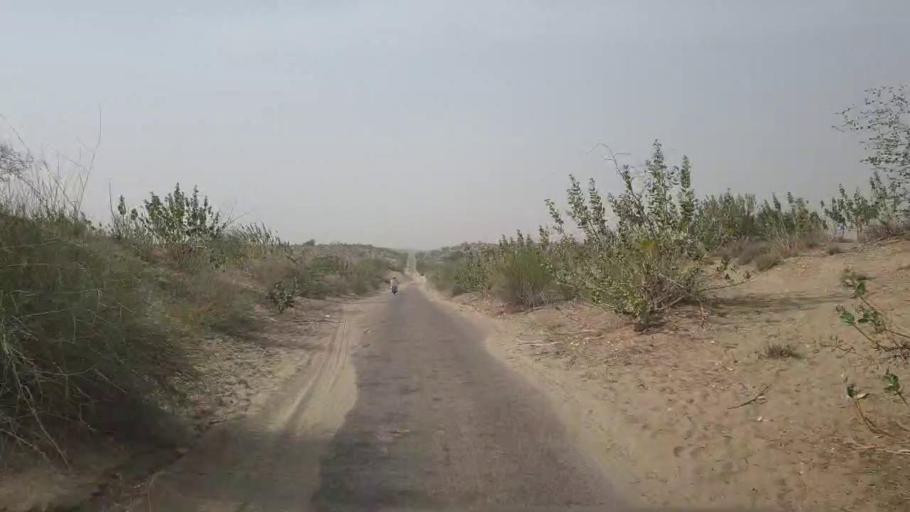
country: PK
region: Sindh
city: Chor
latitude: 25.5969
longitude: 69.9442
